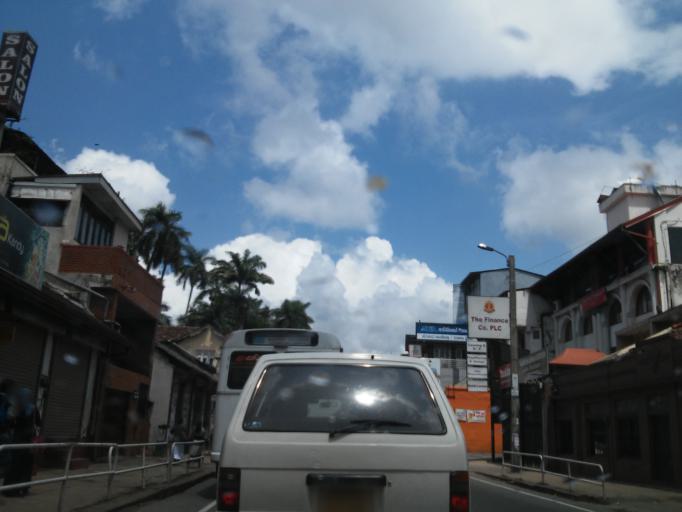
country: LK
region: Central
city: Kandy
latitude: 7.3008
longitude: 80.6363
